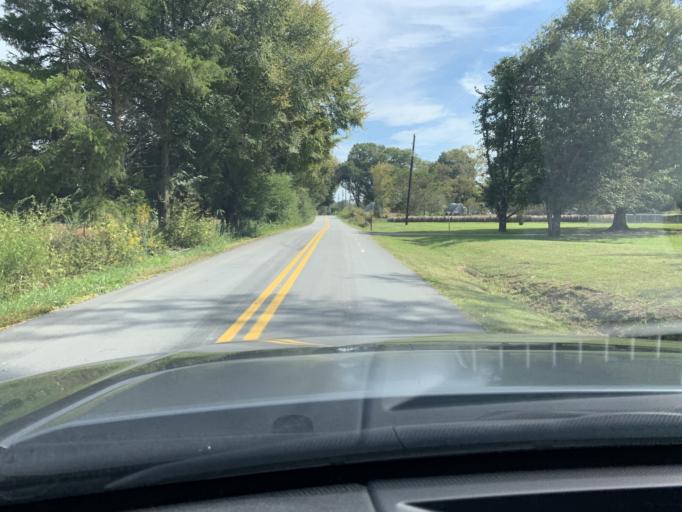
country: US
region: Georgia
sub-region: Floyd County
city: Cave Spring
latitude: 33.9491
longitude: -85.3940
